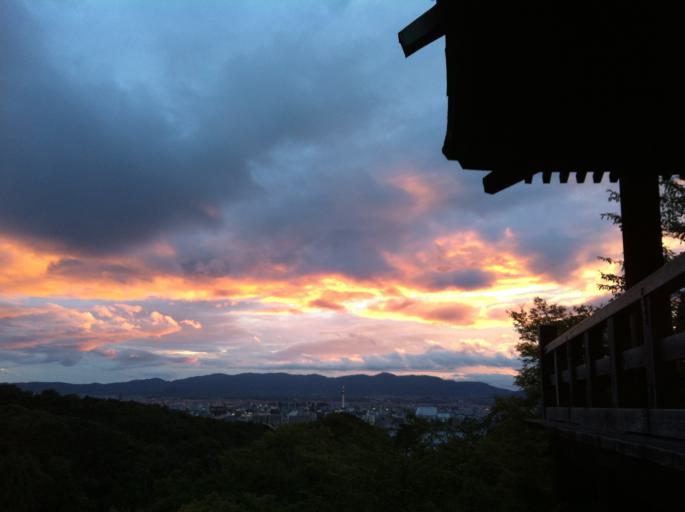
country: JP
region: Kyoto
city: Kyoto
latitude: 34.9944
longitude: 135.7851
